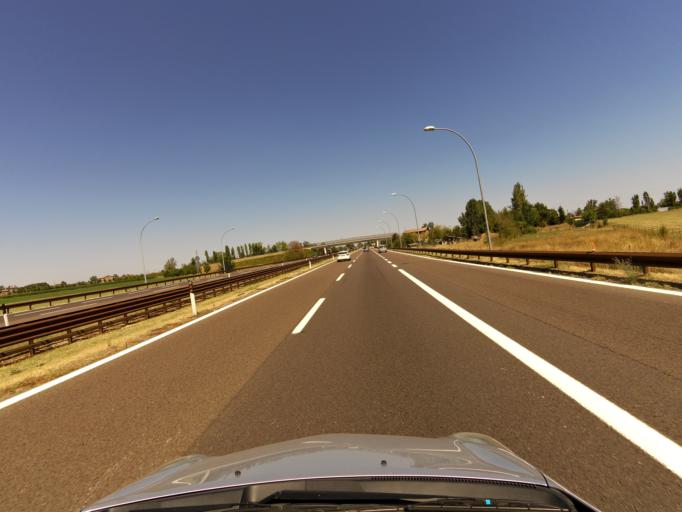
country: IT
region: Emilia-Romagna
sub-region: Provincia di Modena
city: Campogalliano
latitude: 44.7056
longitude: 10.8481
